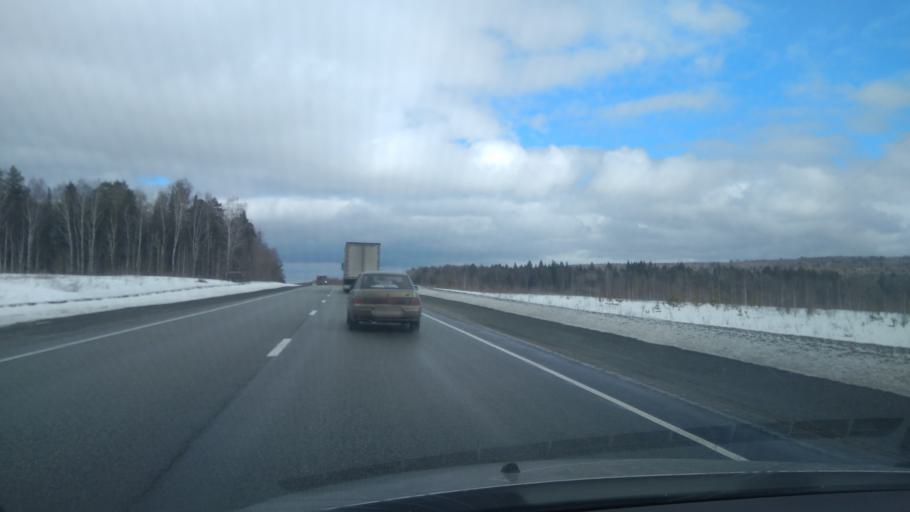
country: RU
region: Sverdlovsk
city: Bisert'
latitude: 56.8123
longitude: 58.7388
